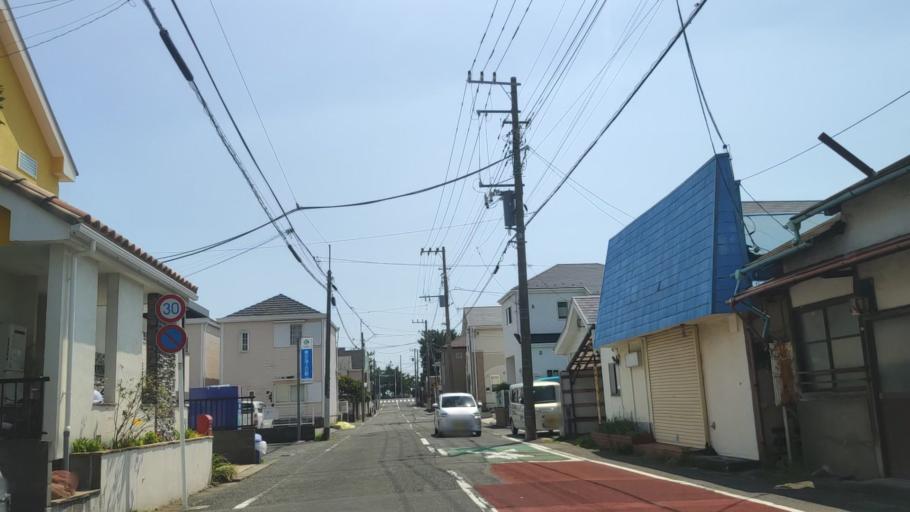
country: JP
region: Kanagawa
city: Hiratsuka
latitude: 35.3165
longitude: 139.3397
